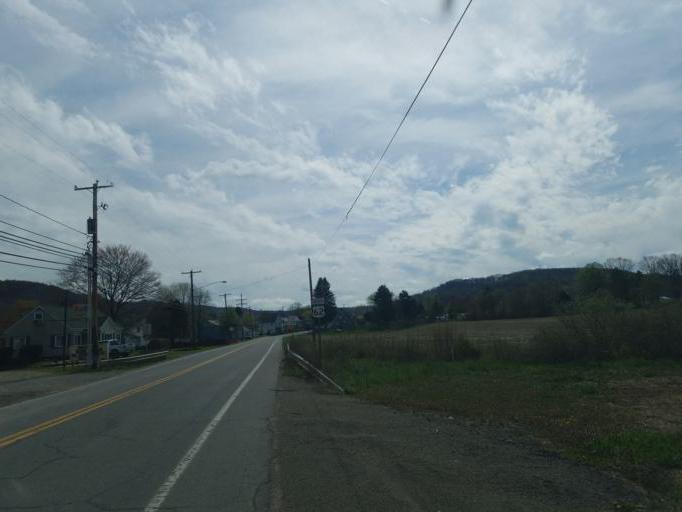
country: US
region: Pennsylvania
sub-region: Venango County
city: Sugarcreek
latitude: 41.3712
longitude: -79.9238
